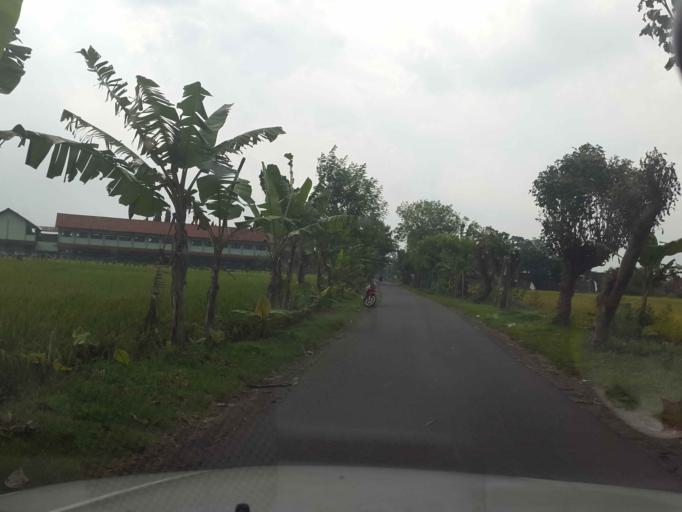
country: ID
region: Central Java
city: Jaten
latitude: -7.5594
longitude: 110.9211
